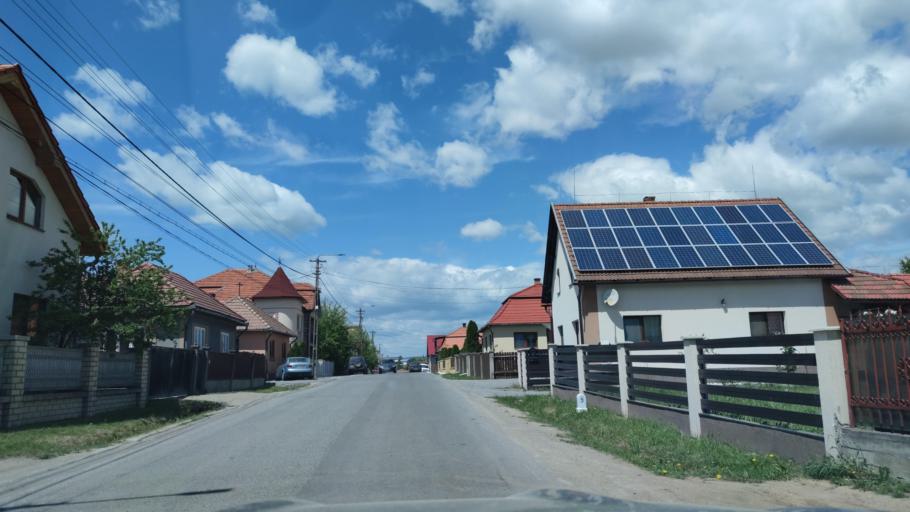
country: RO
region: Harghita
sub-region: Comuna Remetea
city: Remetea
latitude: 46.8062
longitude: 25.4602
